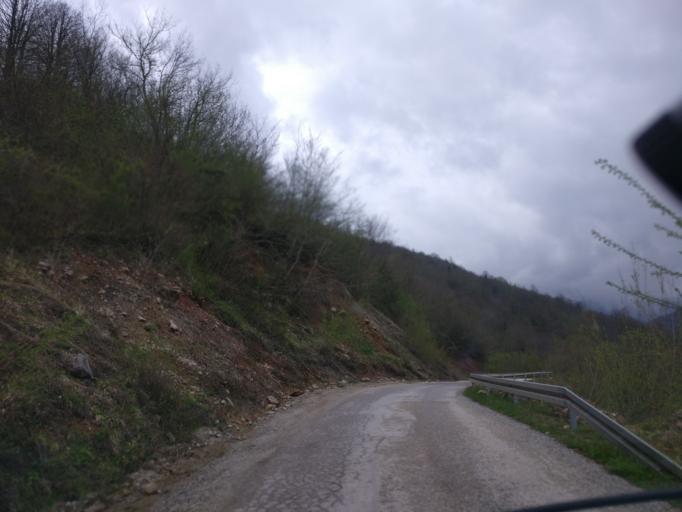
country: BA
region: Republika Srpska
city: Foca
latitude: 43.3590
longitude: 18.8136
